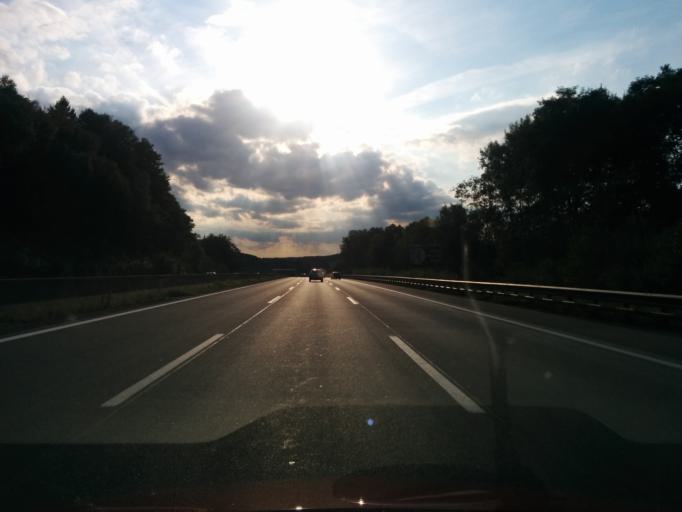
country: AT
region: Lower Austria
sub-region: Politischer Bezirk Amstetten
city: Sankt Georgen am Ybbsfelde
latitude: 48.1393
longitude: 14.9481
